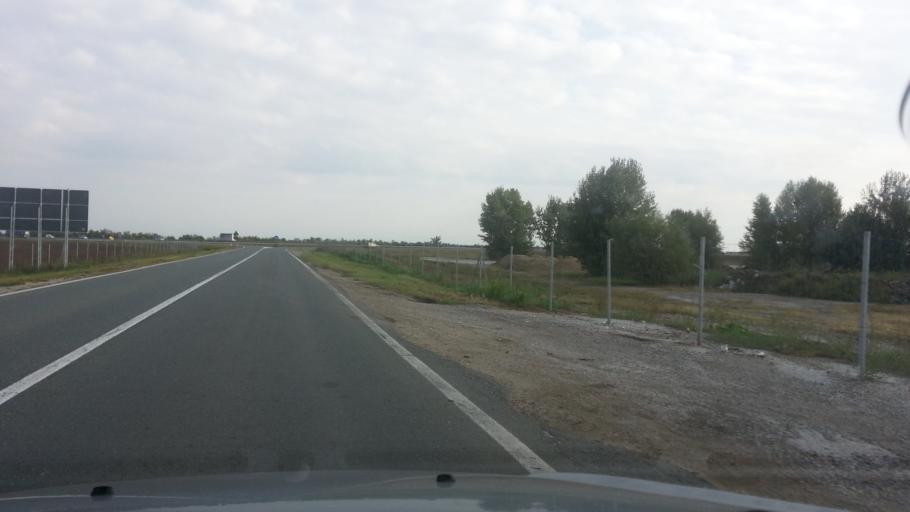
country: RS
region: Autonomna Pokrajina Vojvodina
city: Nova Pazova
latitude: 44.9879
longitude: 20.2106
